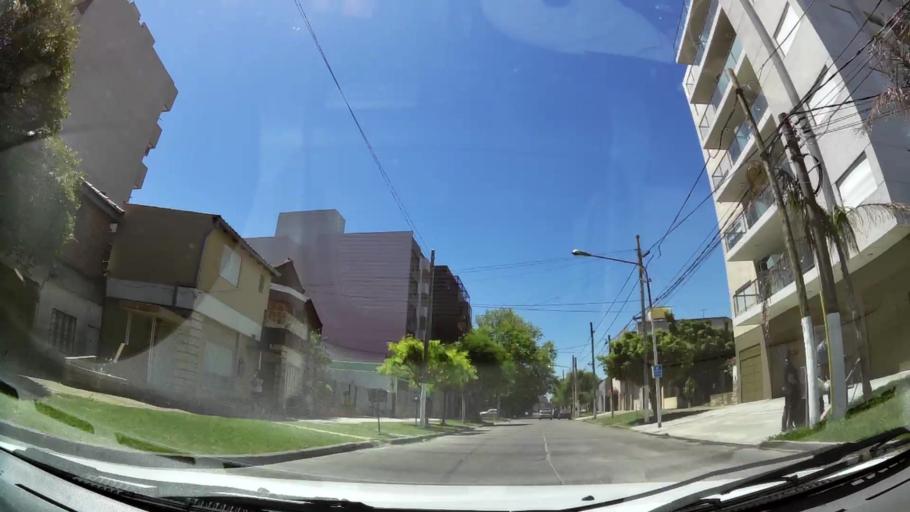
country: AR
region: Buenos Aires
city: Caseros
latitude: -34.5866
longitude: -58.5706
